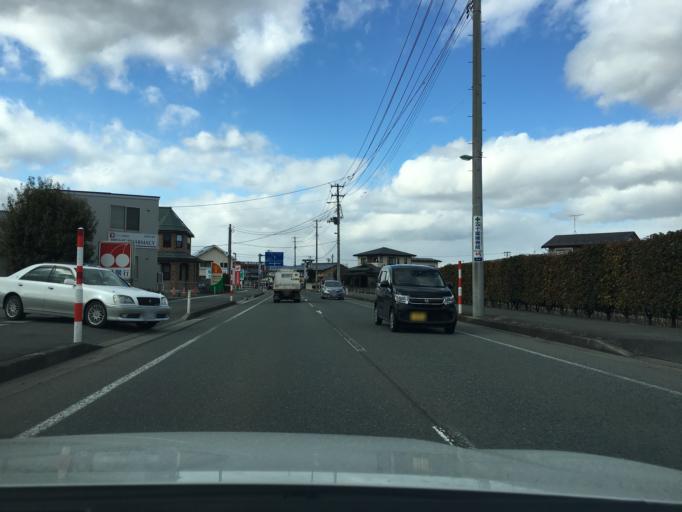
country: JP
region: Yamagata
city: Kaminoyama
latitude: 38.2062
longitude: 140.3081
